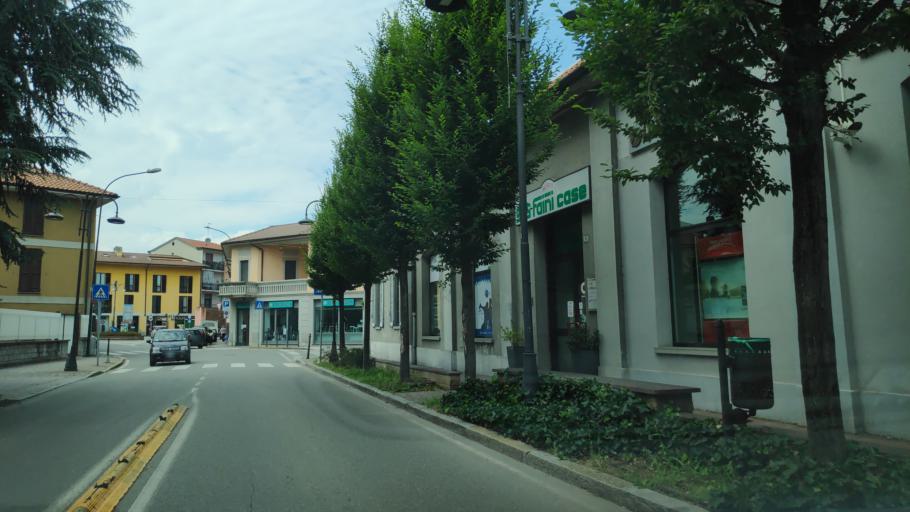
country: IT
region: Lombardy
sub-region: Citta metropolitana di Milano
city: Melzo
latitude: 45.4959
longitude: 9.4232
